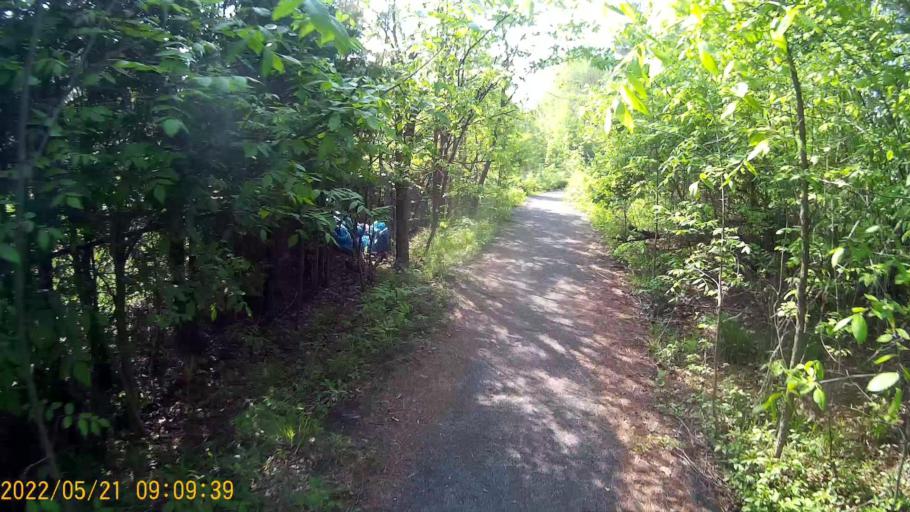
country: CA
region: Ontario
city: Bells Corners
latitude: 45.3224
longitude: -75.9388
